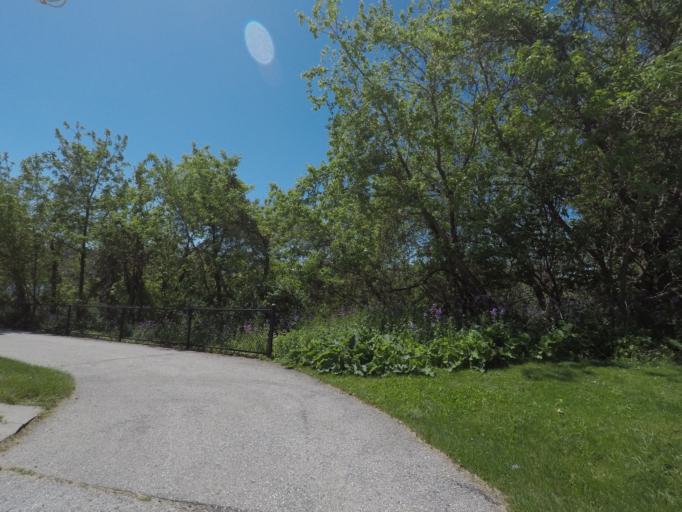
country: US
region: Wisconsin
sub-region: Sheboygan County
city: Sheboygan
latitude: 43.7558
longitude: -87.7239
